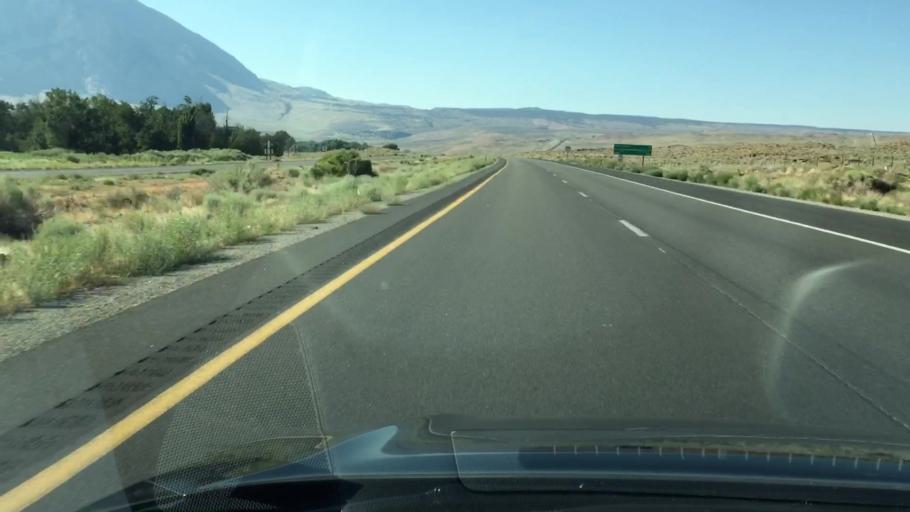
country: US
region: California
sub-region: Inyo County
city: West Bishop
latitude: 37.4212
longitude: -118.5561
